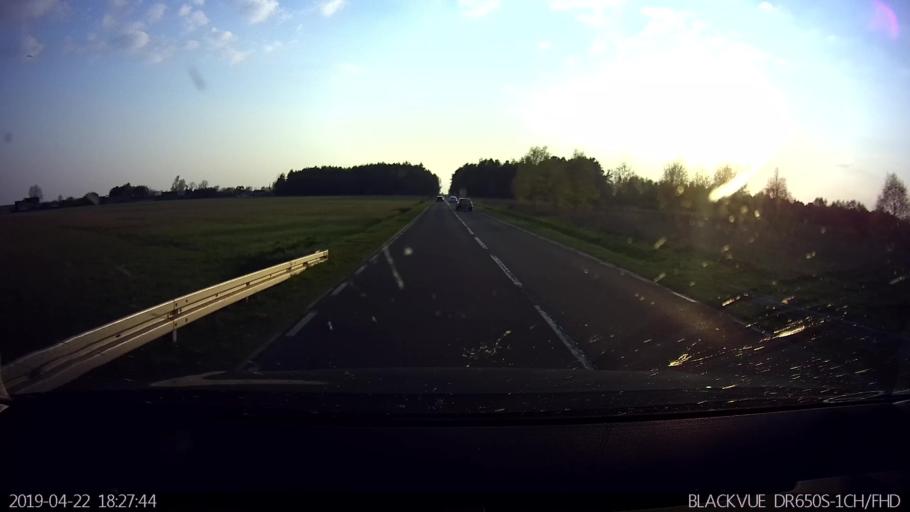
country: PL
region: Masovian Voivodeship
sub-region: Powiat wolominski
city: Tluszcz
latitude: 52.4629
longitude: 21.4902
